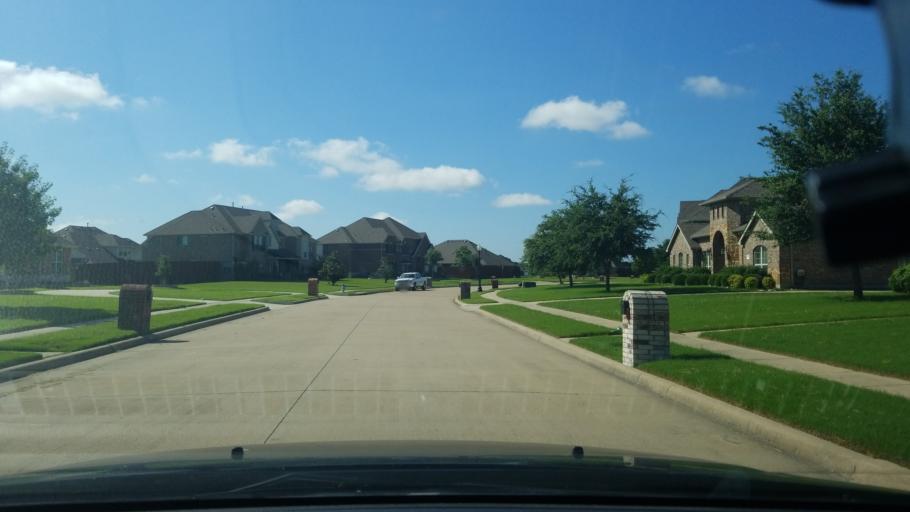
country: US
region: Texas
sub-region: Dallas County
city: Sunnyvale
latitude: 32.8056
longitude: -96.5833
